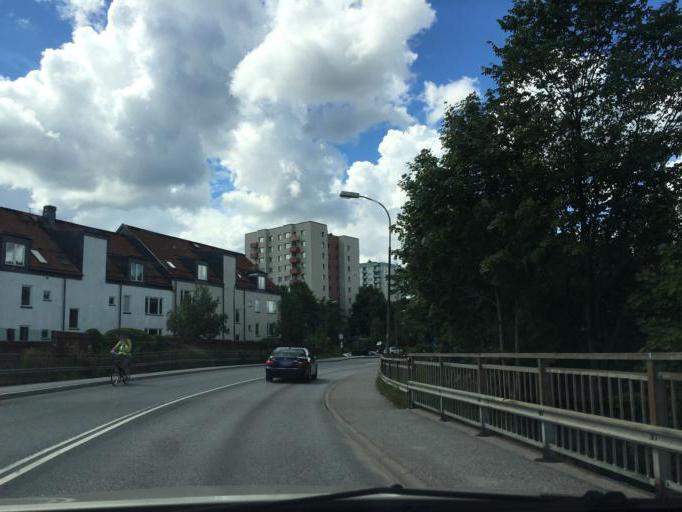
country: SE
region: Stockholm
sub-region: Nacka Kommun
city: Nacka
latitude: 59.3065
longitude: 18.1506
